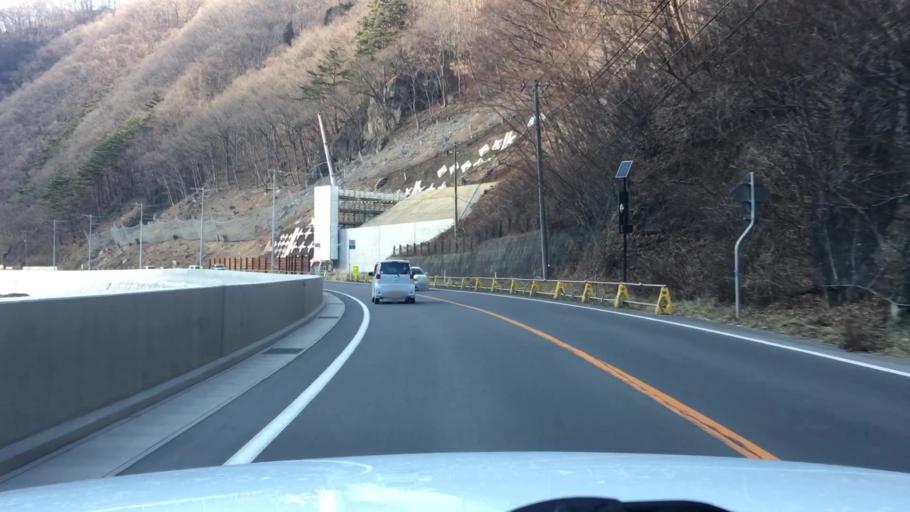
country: JP
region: Iwate
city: Miyako
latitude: 39.5981
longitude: 141.7582
